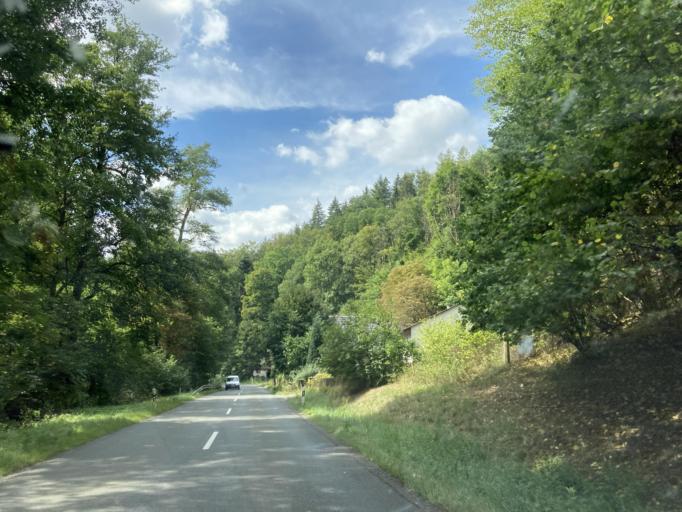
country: DE
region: Bavaria
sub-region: Upper Franconia
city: Kupferberg
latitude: 50.1498
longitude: 11.5613
